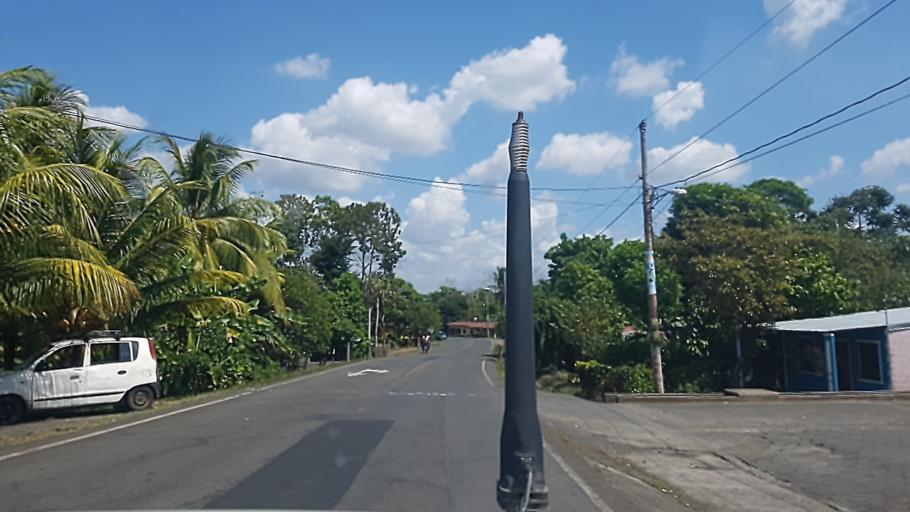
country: NI
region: Atlantico Sur
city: Muelle de los Bueyes
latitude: 11.9153
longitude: -84.6449
